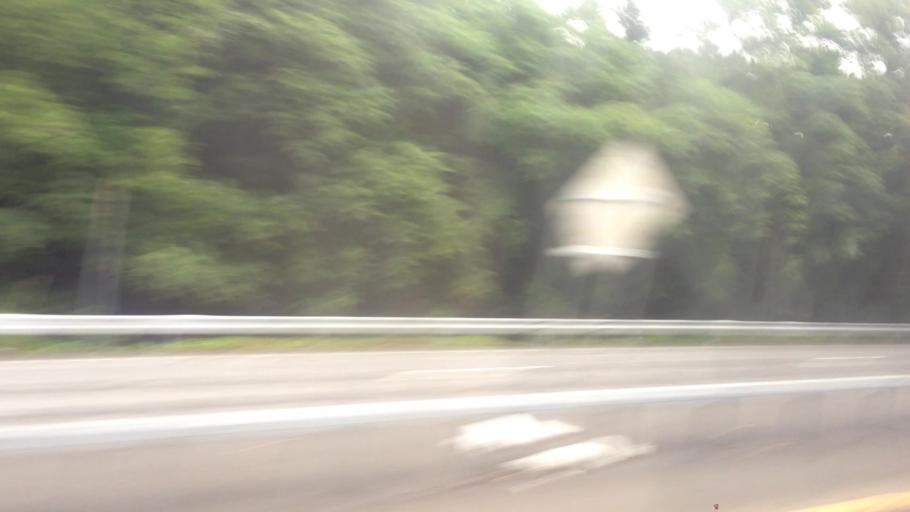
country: US
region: New York
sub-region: Ulster County
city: Lake Katrine
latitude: 41.9760
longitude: -73.9757
